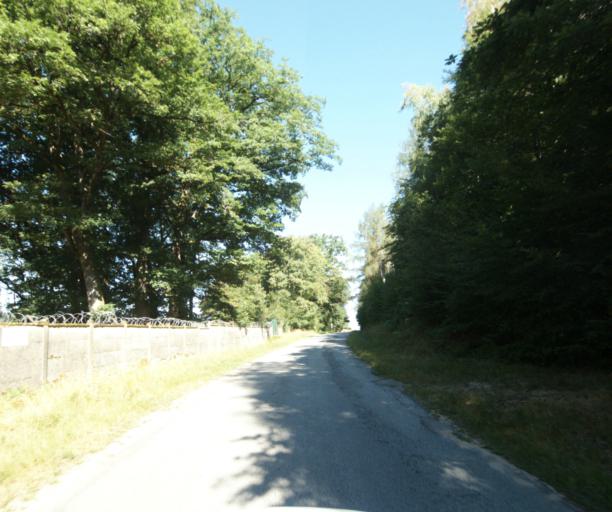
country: FR
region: Lorraine
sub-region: Departement des Vosges
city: Epinal
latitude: 48.1550
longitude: 6.4641
